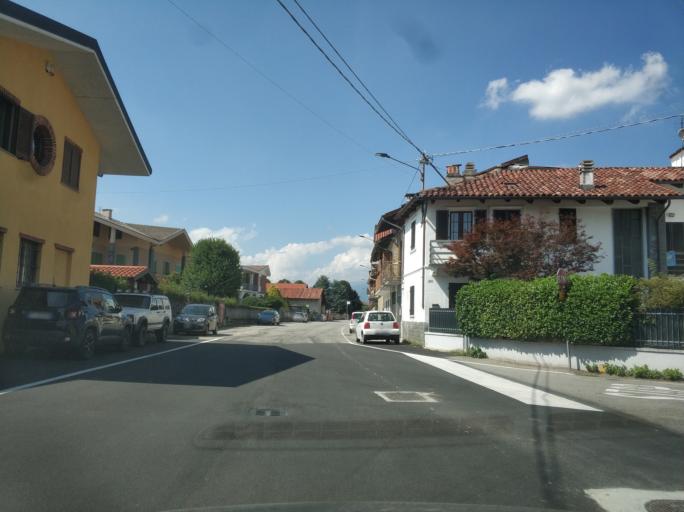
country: IT
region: Piedmont
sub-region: Provincia di Torino
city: Feletto
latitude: 45.2927
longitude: 7.7227
